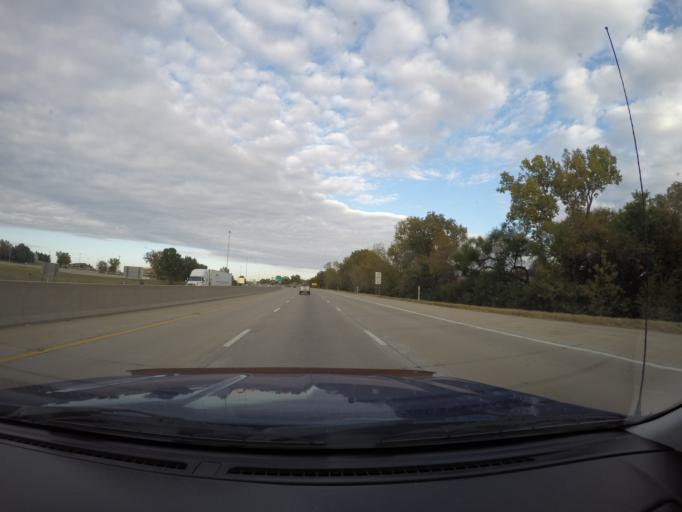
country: US
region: Kansas
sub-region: Shawnee County
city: Topeka
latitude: 39.0545
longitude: -95.7539
